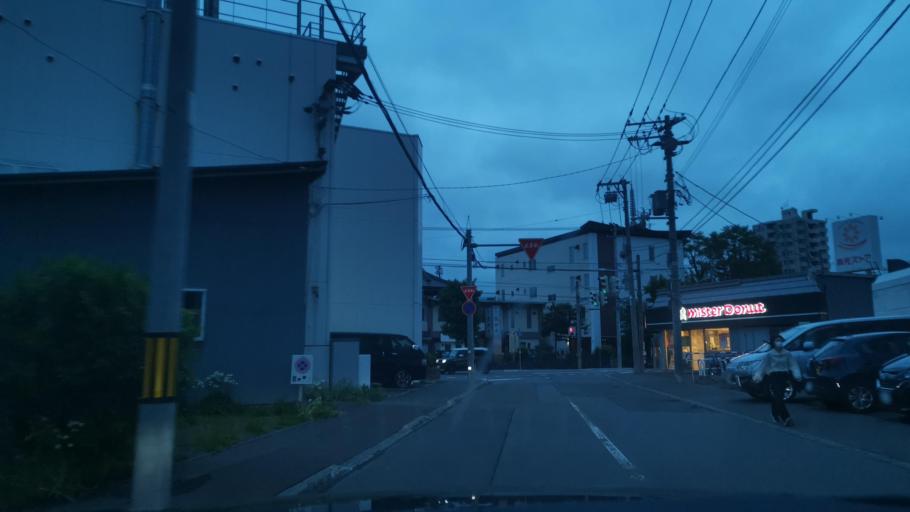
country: JP
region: Hokkaido
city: Sapporo
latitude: 43.0621
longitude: 141.3133
